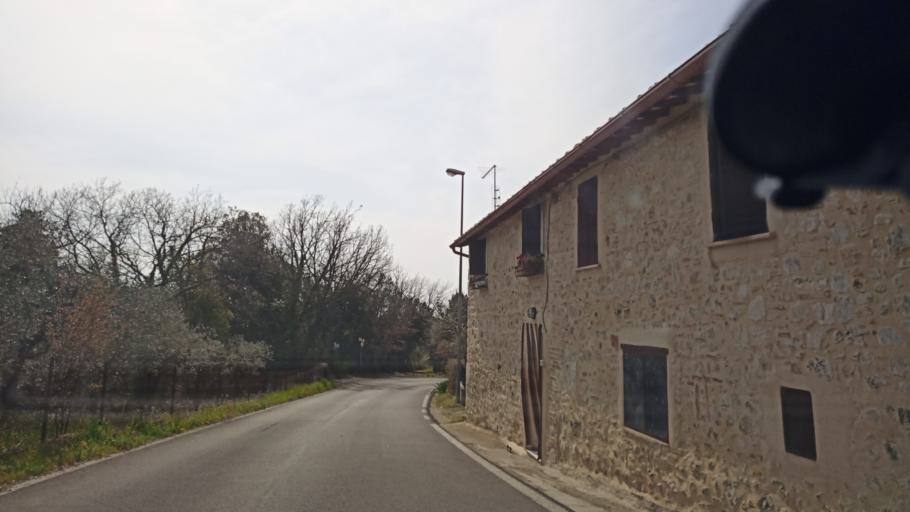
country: IT
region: Latium
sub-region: Provincia di Rieti
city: Montasola
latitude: 42.3659
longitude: 12.6763
